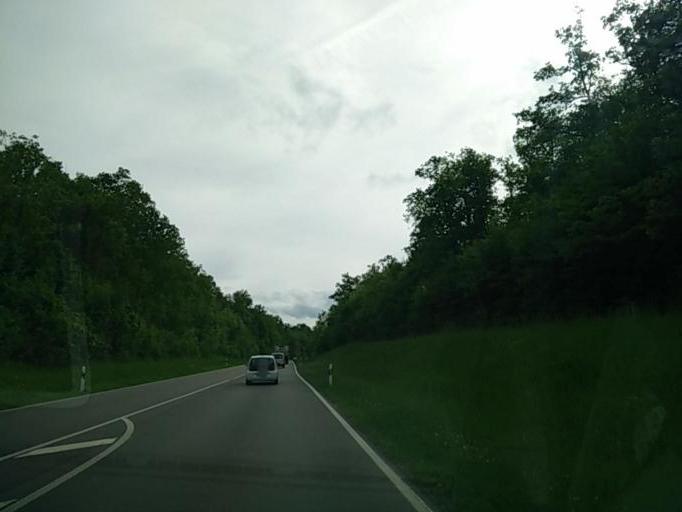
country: DE
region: Baden-Wuerttemberg
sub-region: Regierungsbezirk Stuttgart
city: Ehningen
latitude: 48.6733
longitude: 8.9742
